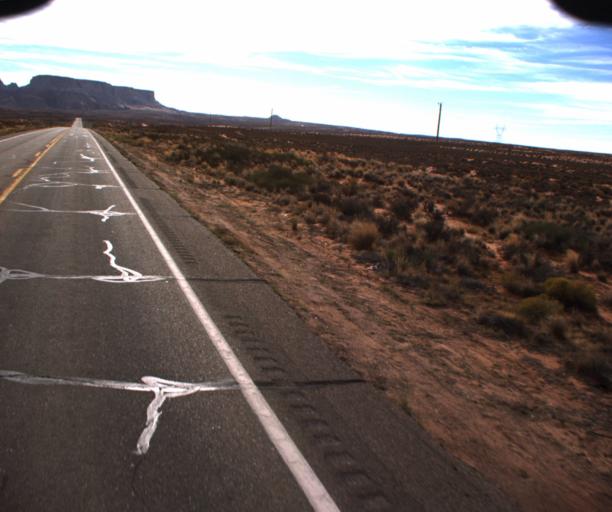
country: US
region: Arizona
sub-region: Coconino County
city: LeChee
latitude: 36.8857
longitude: -111.3594
